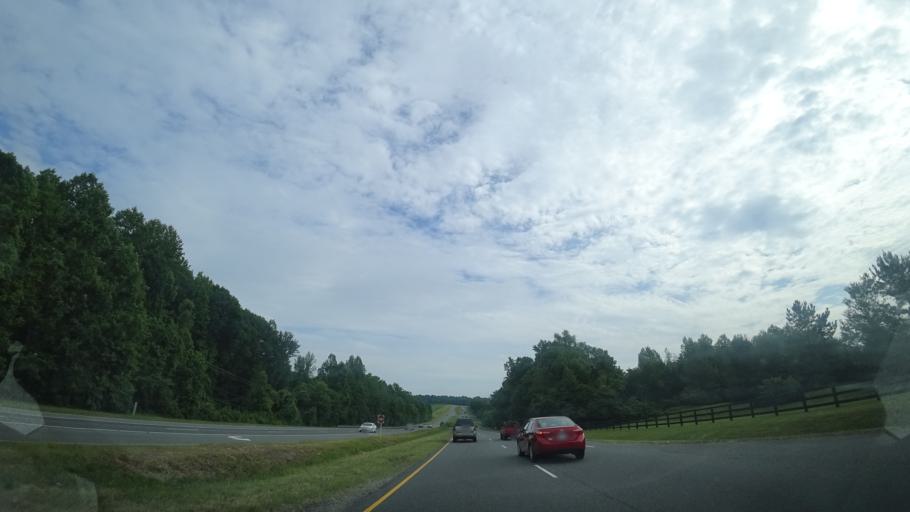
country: US
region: Virginia
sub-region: Spotsylvania County
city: Spotsylvania
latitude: 38.2155
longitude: -77.5709
